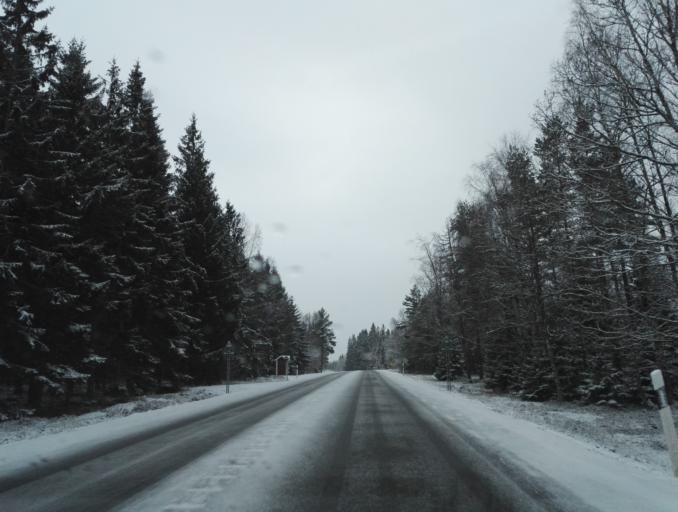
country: SE
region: Kronoberg
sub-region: Uppvidinge Kommun
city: Lenhovda
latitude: 57.0648
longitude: 15.1927
